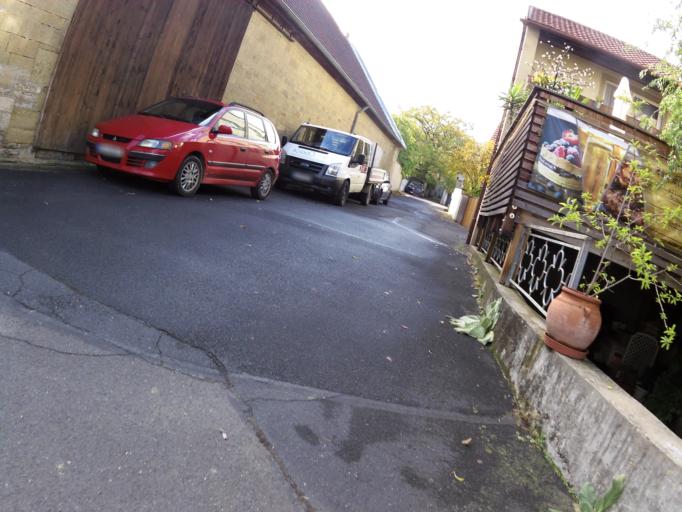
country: DE
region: Bavaria
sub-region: Regierungsbezirk Unterfranken
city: Frickenhausen
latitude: 49.7052
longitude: 10.0809
